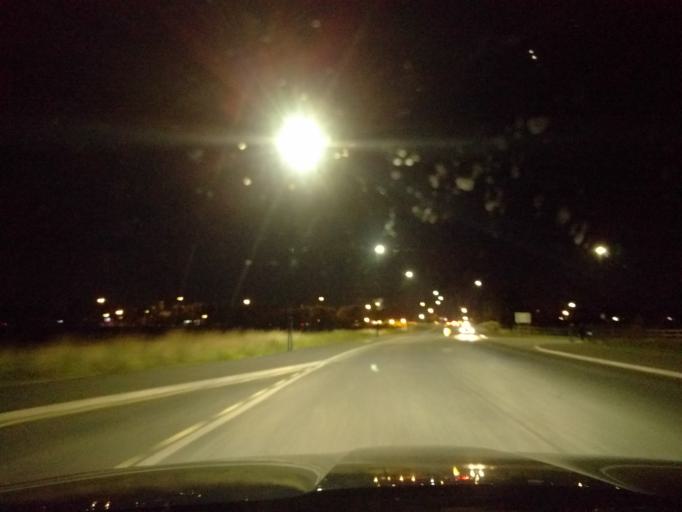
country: GB
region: England
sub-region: Borough of North Tyneside
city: Wallsend
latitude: 55.0125
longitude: -1.5490
